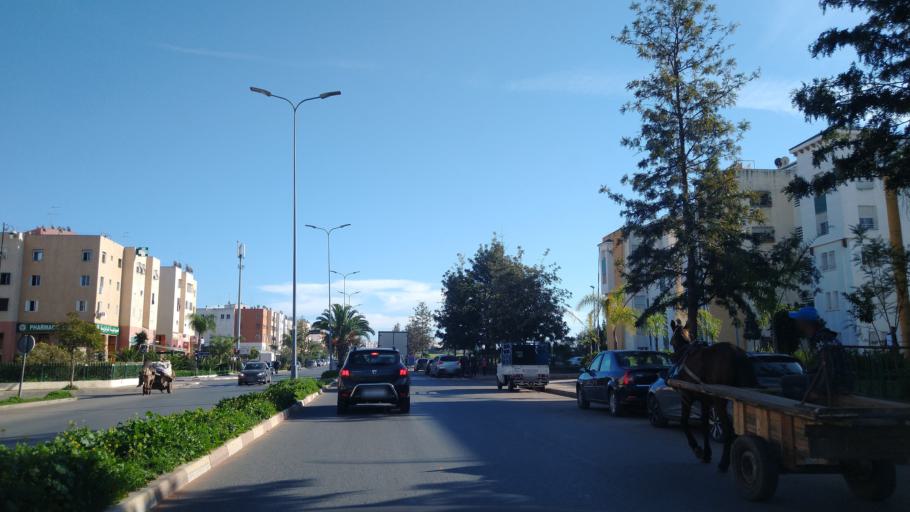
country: MA
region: Rabat-Sale-Zemmour-Zaer
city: Sale
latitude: 33.9943
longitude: -6.7450
